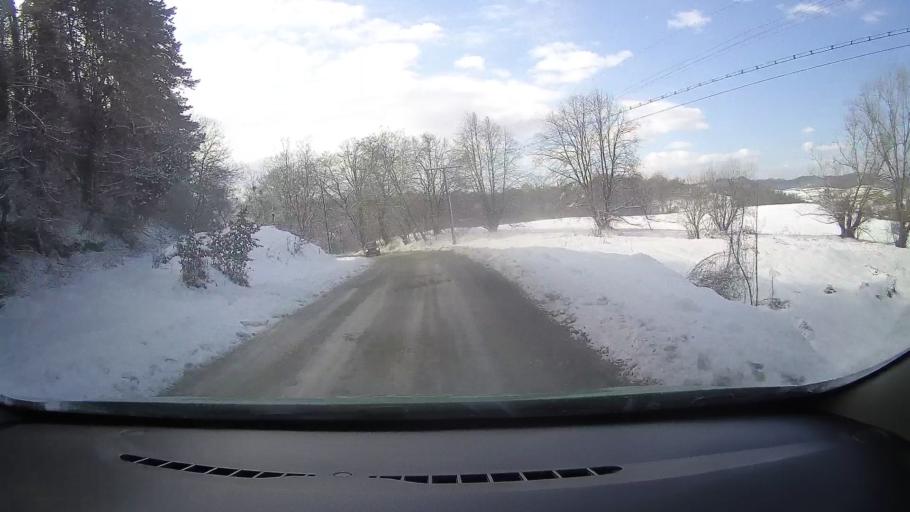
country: RO
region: Sibiu
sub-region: Comuna Mosna
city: Mosna
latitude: 46.0179
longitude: 24.4103
